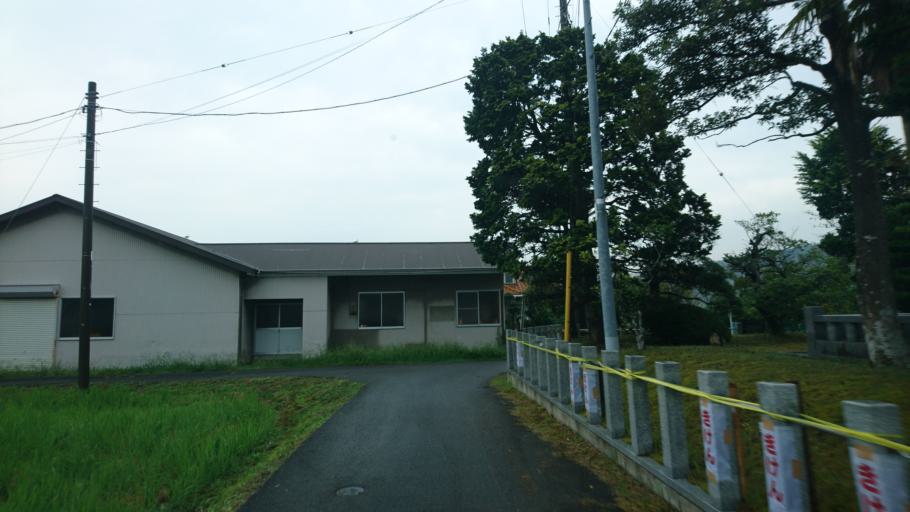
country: JP
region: Chiba
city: Kimitsu
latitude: 35.2908
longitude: 139.9864
